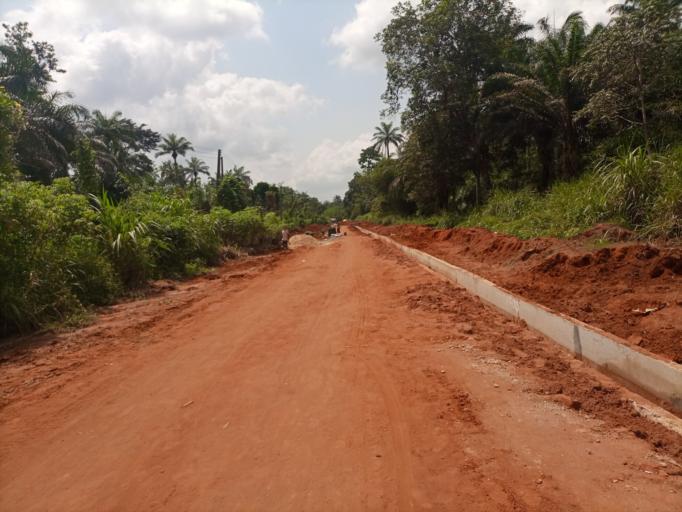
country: NG
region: Abia
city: Umuahia
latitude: 5.4801
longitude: 7.3295
